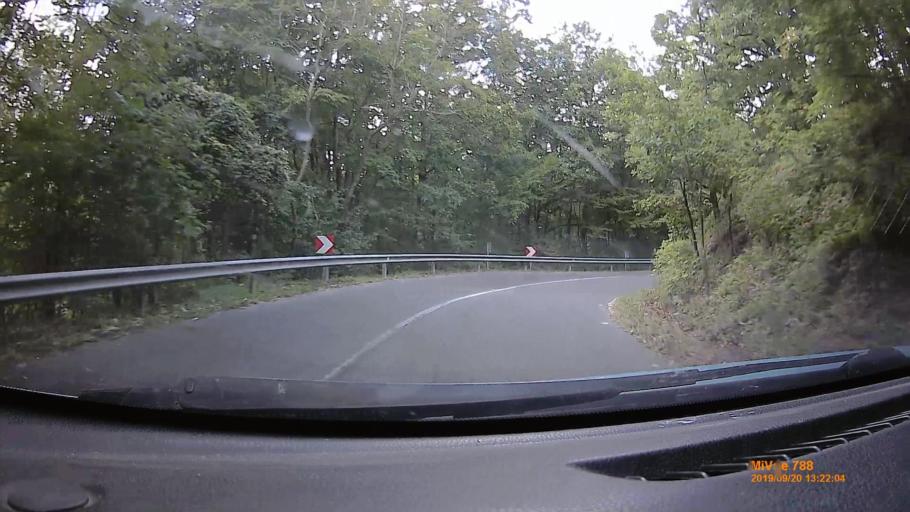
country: HU
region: Heves
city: Felsotarkany
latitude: 48.0259
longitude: 20.4754
